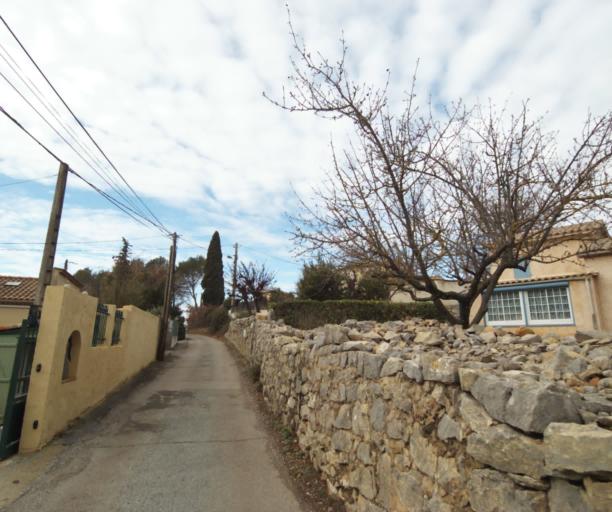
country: FR
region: Provence-Alpes-Cote d'Azur
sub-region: Departement du Var
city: Trans-en-Provence
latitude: 43.5186
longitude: 6.4878
